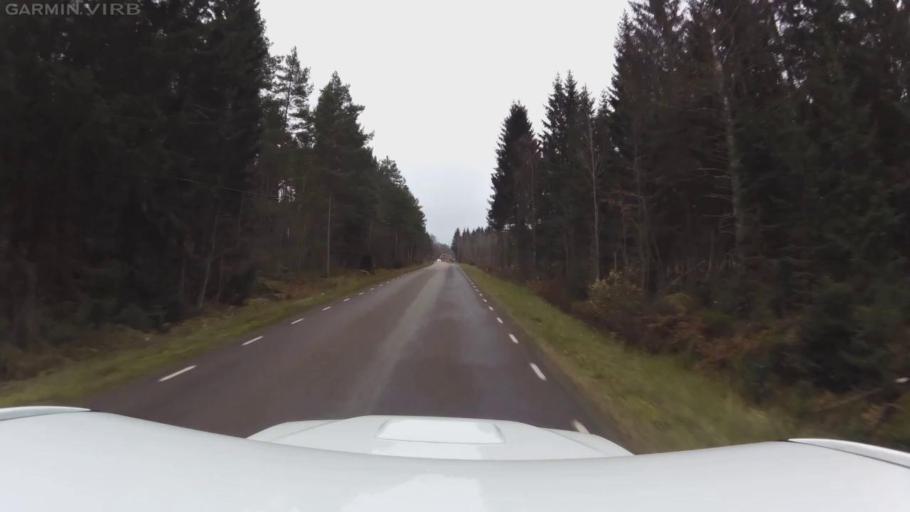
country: SE
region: OEstergoetland
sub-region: Linkopings Kommun
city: Vikingstad
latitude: 58.2352
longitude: 15.3900
